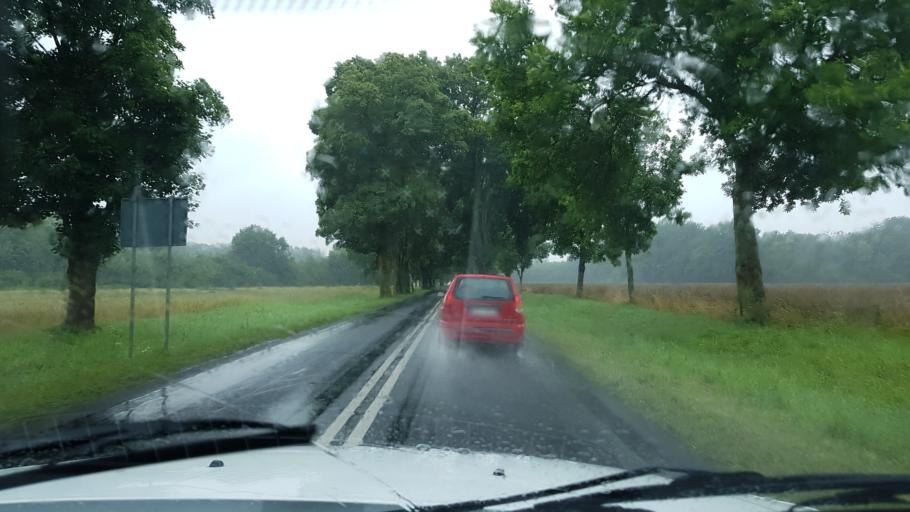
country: PL
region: West Pomeranian Voivodeship
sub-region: Powiat goleniowski
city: Nowogard
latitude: 53.6057
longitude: 15.1558
